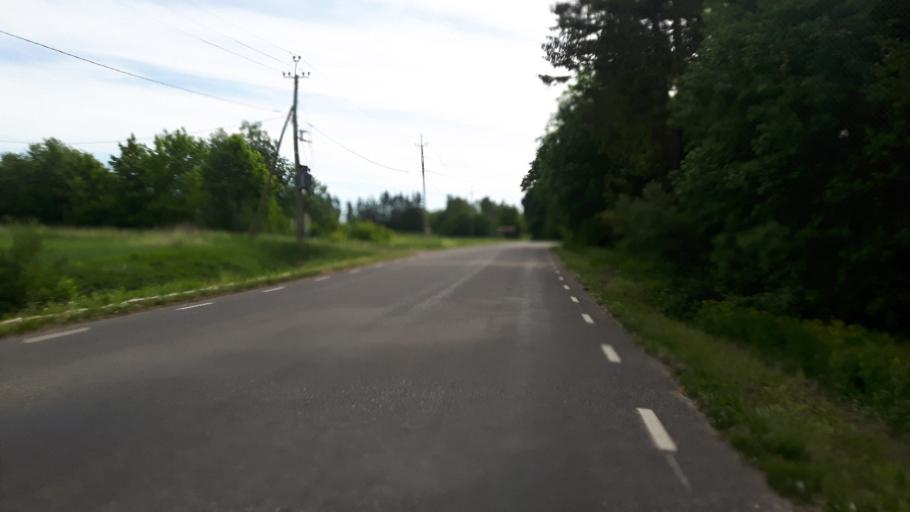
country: EE
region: Harju
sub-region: Maardu linn
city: Maardu
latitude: 59.4236
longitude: 25.0129
